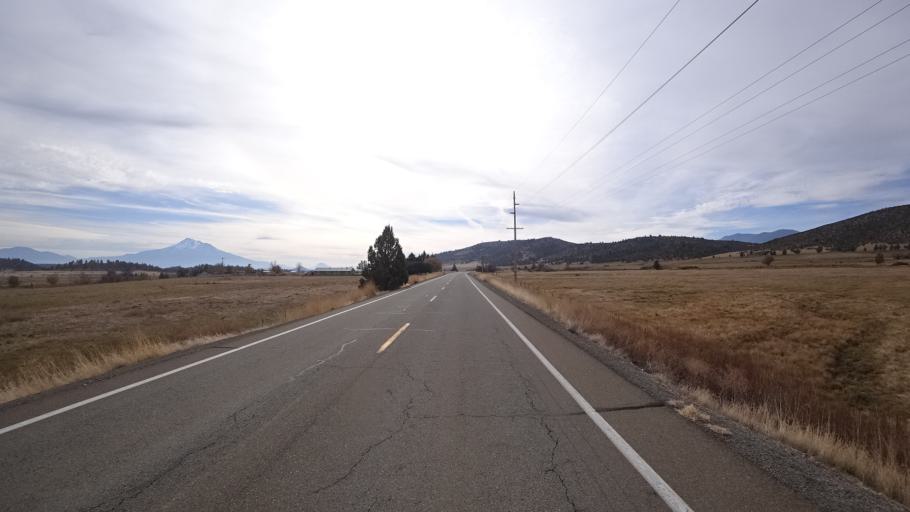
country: US
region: California
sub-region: Siskiyou County
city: Montague
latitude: 41.6930
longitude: -122.5350
